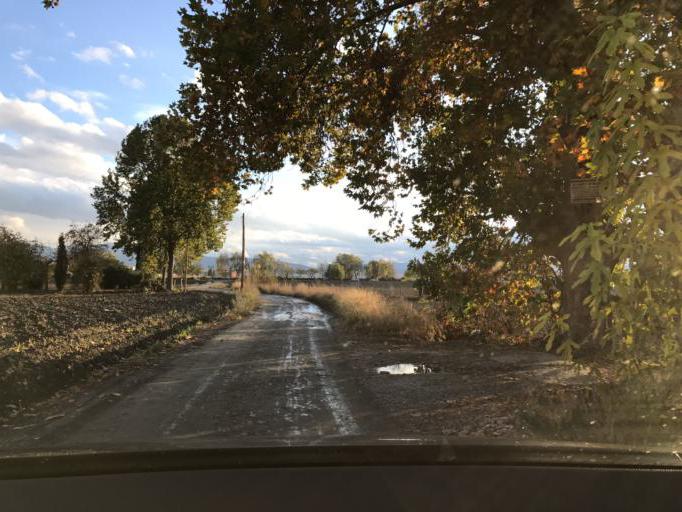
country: ES
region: Andalusia
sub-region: Provincia de Granada
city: Armilla
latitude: 37.1641
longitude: -3.6136
